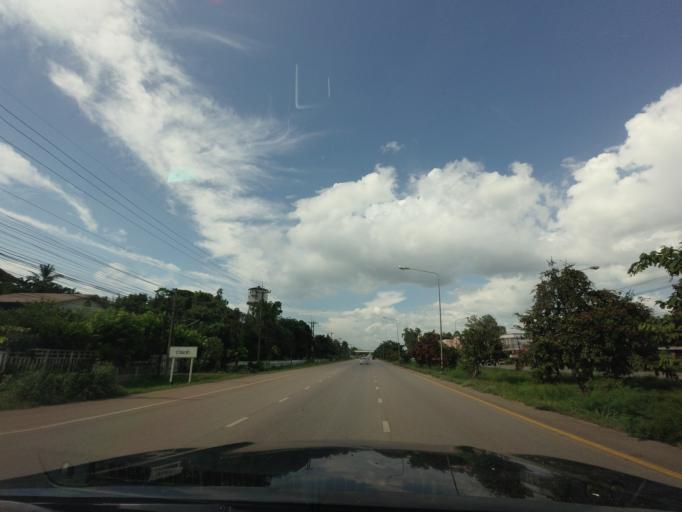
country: TH
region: Changwat Udon Thani
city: Udon Thani
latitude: 17.5495
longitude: 102.8007
